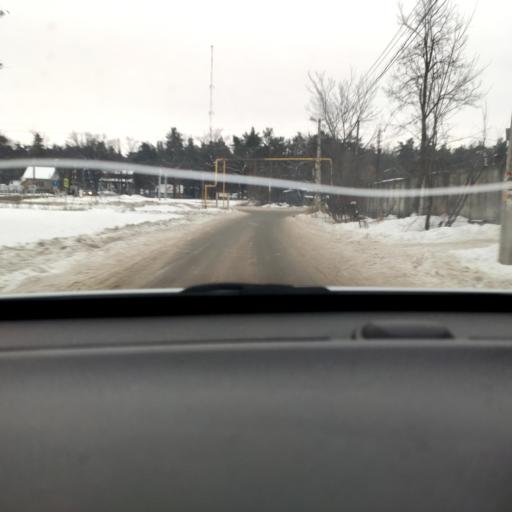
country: RU
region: Voronezj
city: Somovo
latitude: 51.7476
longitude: 39.3800
